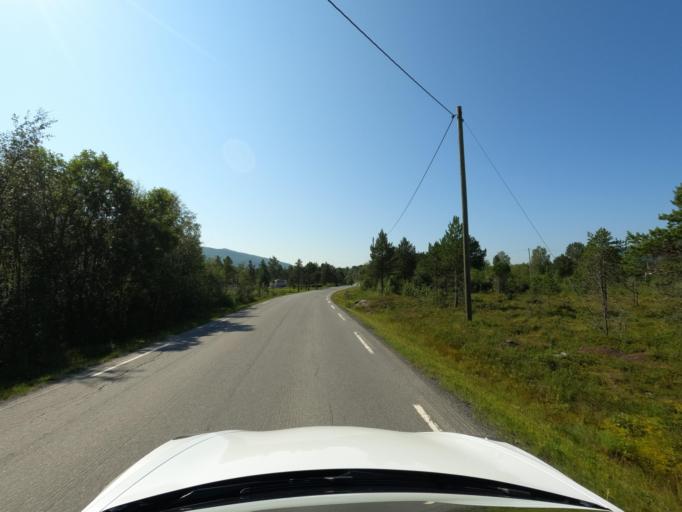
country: NO
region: Nordland
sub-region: Ballangen
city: Ballangen
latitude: 68.3564
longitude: 16.8696
